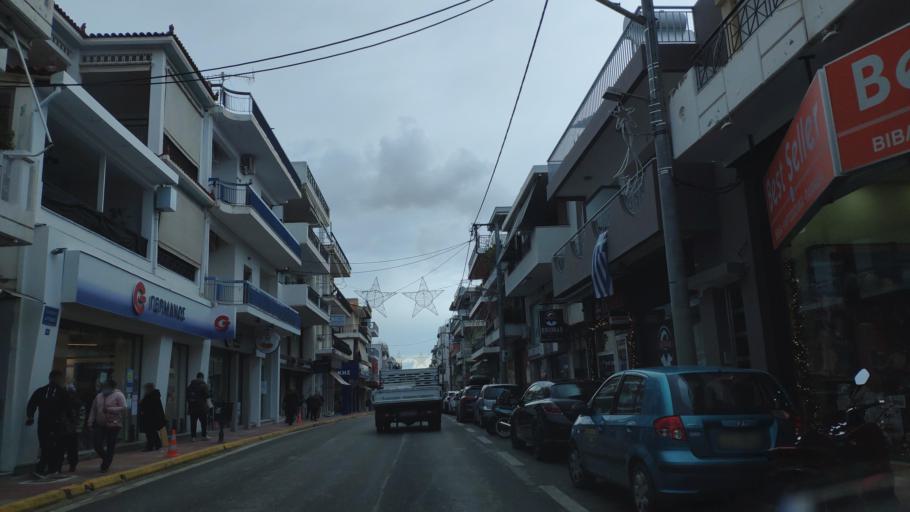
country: GR
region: Attica
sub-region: Nomarchia Anatolikis Attikis
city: Artemida
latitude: 37.9755
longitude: 24.0084
